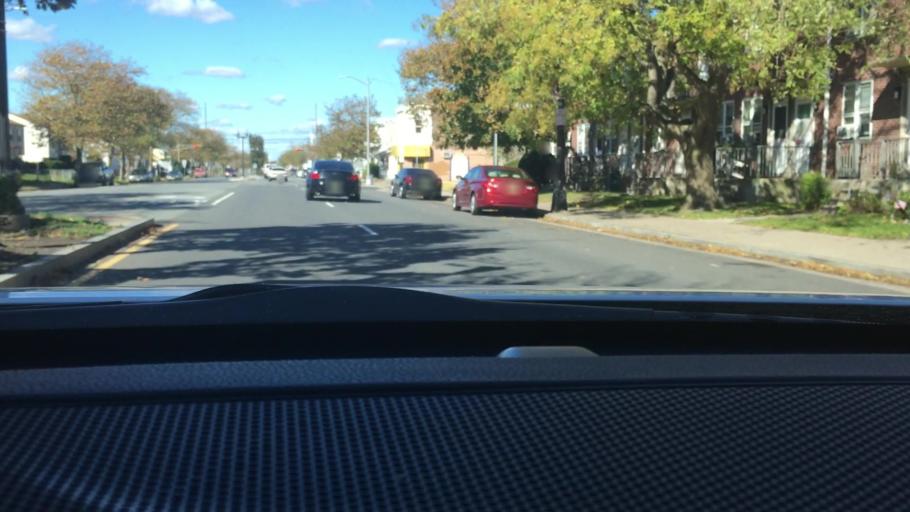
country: US
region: New Jersey
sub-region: Atlantic County
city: Atlantic City
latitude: 39.3655
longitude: -74.4352
